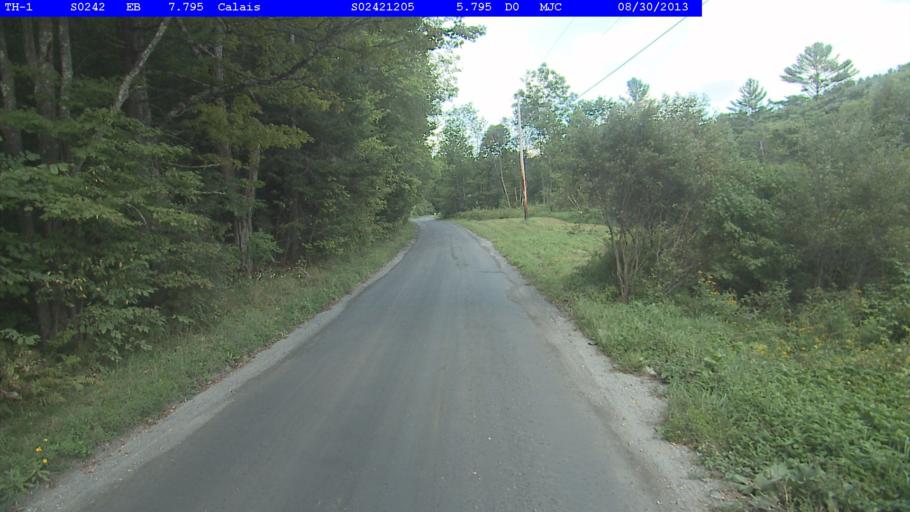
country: US
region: Vermont
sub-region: Caledonia County
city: Hardwick
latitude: 44.3874
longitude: -72.4509
